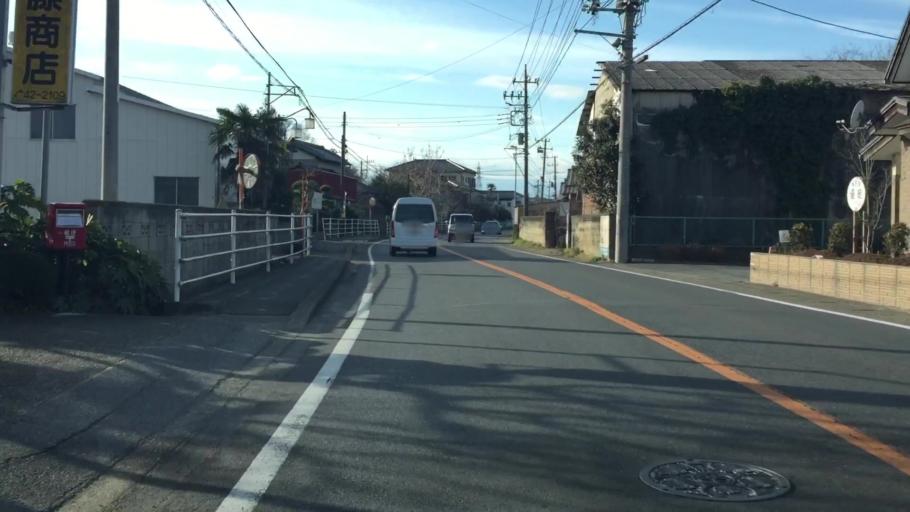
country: JP
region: Chiba
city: Shiroi
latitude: 35.8310
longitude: 140.1208
